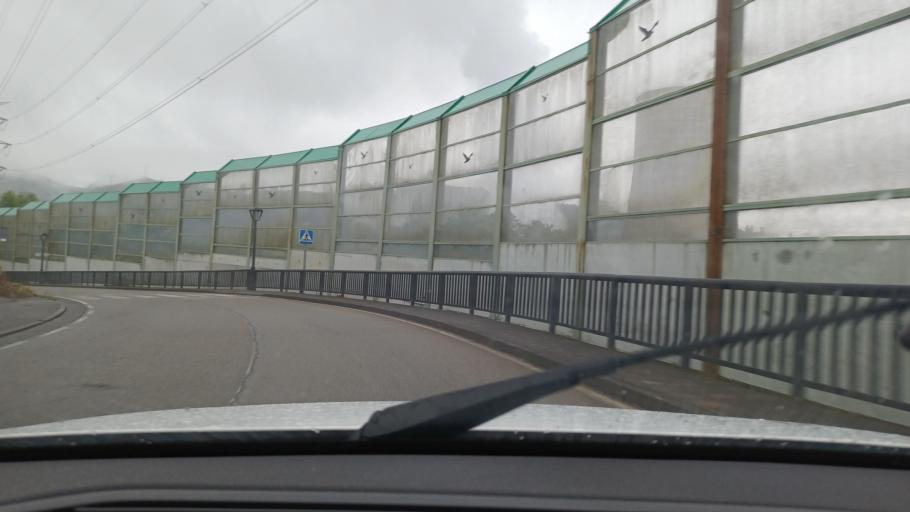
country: ES
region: Asturias
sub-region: Province of Asturias
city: Castandiello
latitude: 43.3111
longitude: -5.8748
